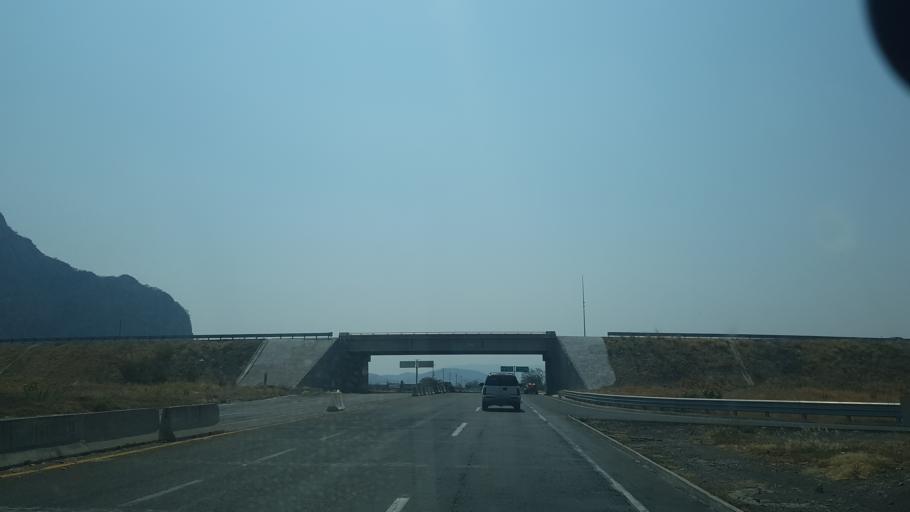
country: MX
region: Morelos
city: Jantetelco
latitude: 18.7030
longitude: -98.7694
